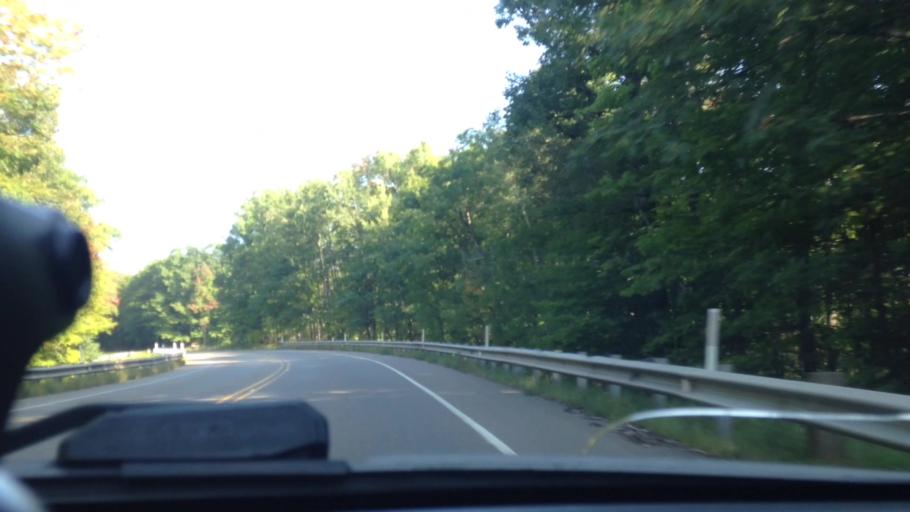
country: US
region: Michigan
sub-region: Dickinson County
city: Quinnesec
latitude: 45.8200
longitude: -87.9886
